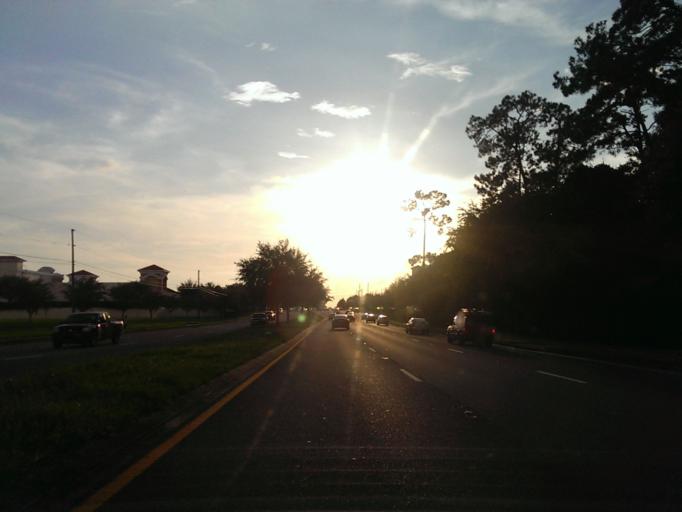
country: US
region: Florida
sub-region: Orange County
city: Tangelo Park
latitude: 28.4938
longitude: -81.4717
